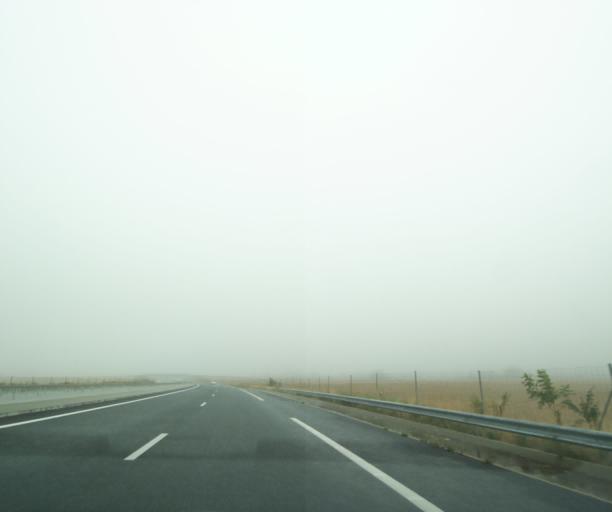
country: FR
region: Midi-Pyrenees
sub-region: Departement de l'Aveyron
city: Naucelle
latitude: 44.1805
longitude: 2.3581
